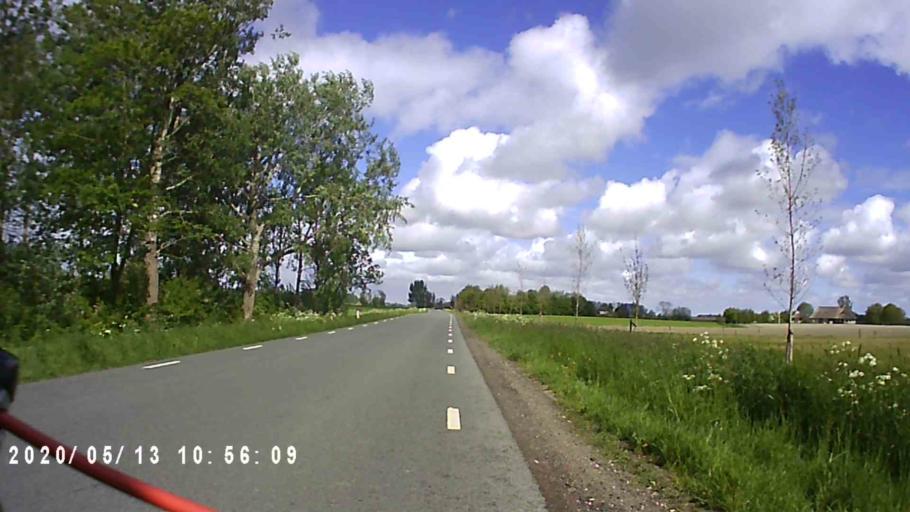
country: NL
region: Groningen
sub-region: Gemeente Zuidhorn
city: Grijpskerk
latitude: 53.2694
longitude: 6.3368
